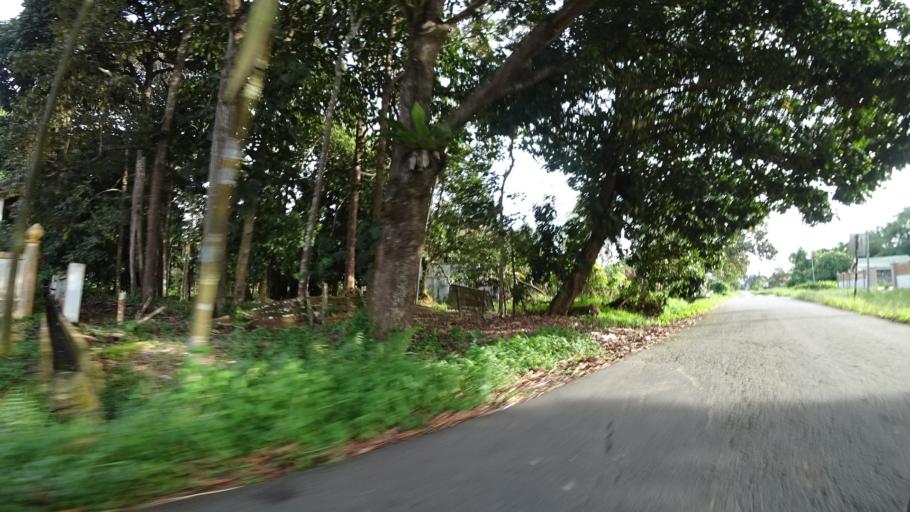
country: BN
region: Brunei and Muara
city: Bandar Seri Begawan
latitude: 4.8091
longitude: 114.8281
